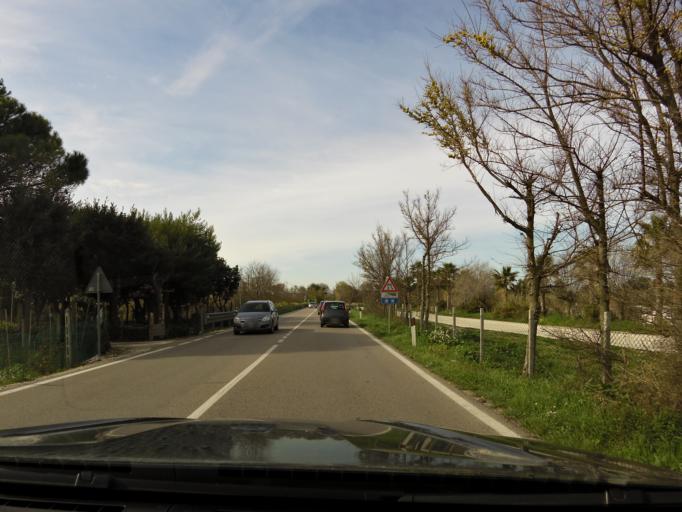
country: IT
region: The Marches
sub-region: Provincia di Macerata
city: Porto Potenza Picena
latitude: 43.3928
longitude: 13.6809
